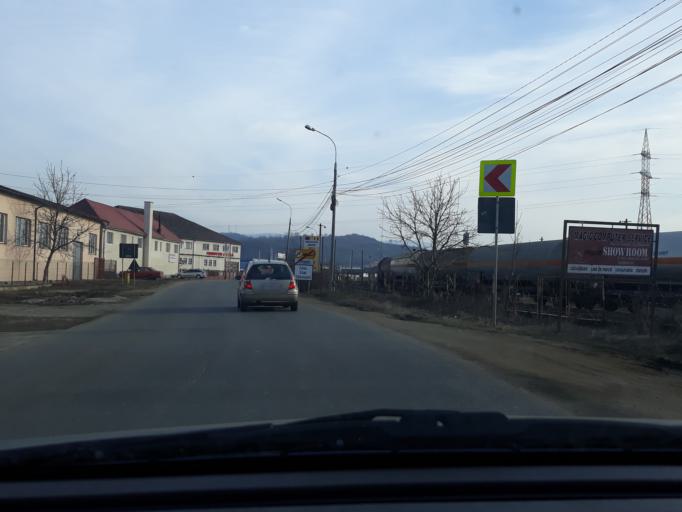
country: RO
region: Salaj
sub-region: Comuna Criseni
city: Criseni
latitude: 47.2233
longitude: 23.0398
